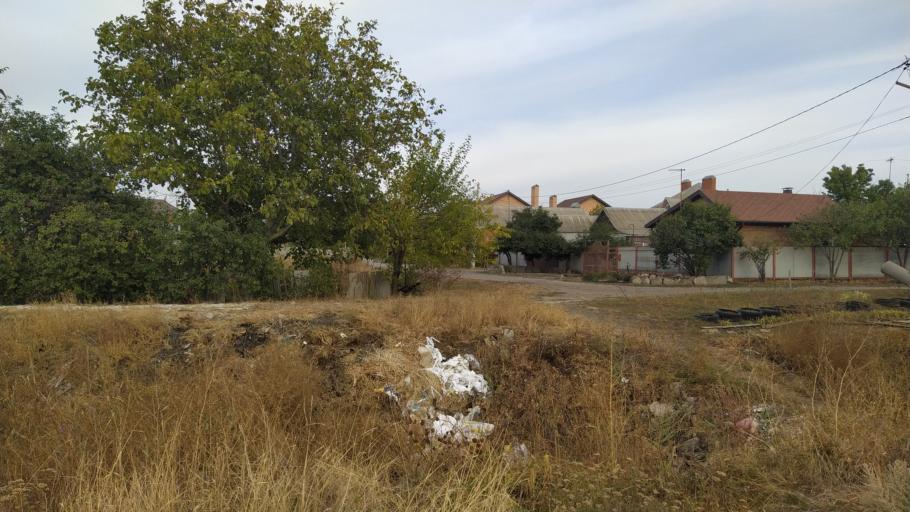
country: RU
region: Rostov
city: Bataysk
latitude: 47.1093
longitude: 39.6838
